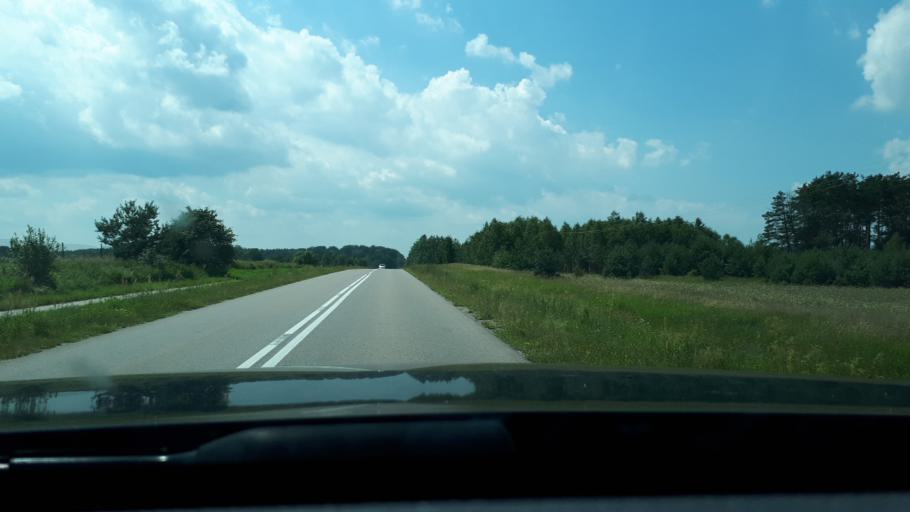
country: PL
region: Podlasie
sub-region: Powiat bialostocki
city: Choroszcz
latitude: 53.1256
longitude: 22.9700
